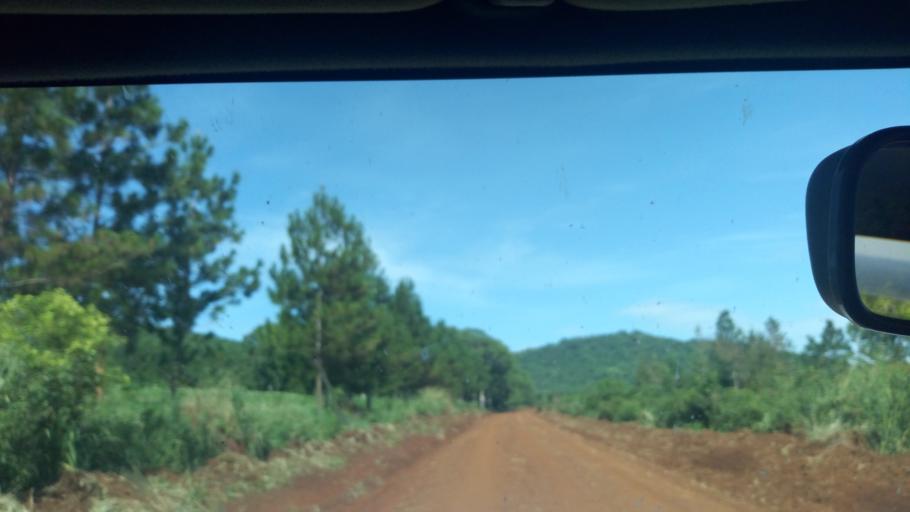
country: UG
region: Western Region
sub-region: Masindi District
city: Masindi
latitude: 1.6515
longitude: 31.7829
